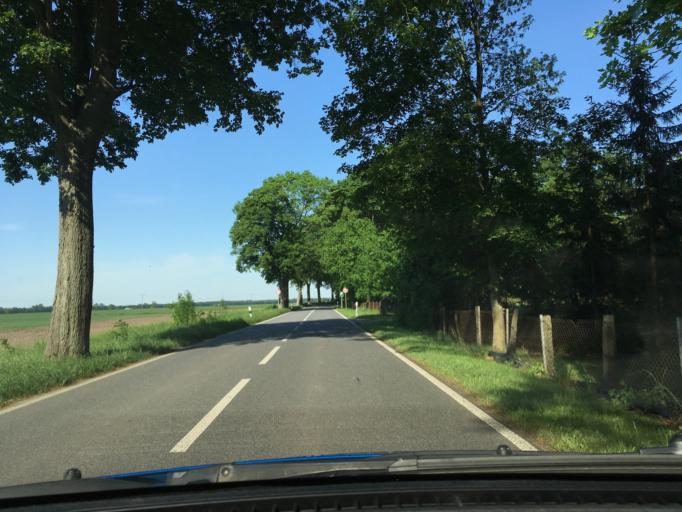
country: DE
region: Lower Saxony
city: Gorleben
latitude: 53.0794
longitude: 11.4054
